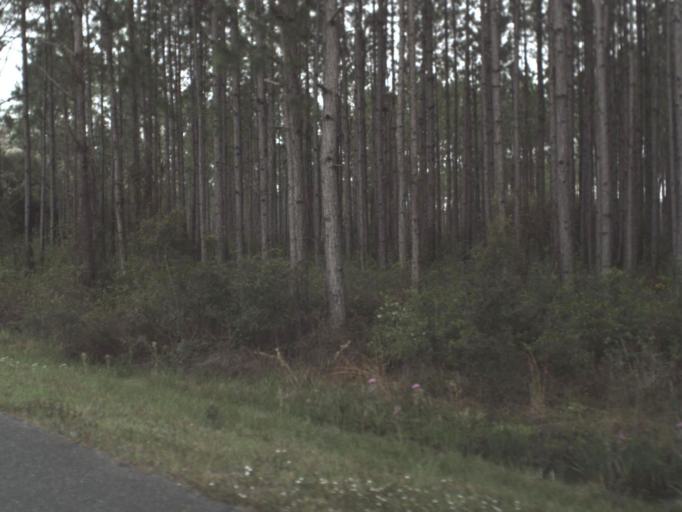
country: US
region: Florida
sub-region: Franklin County
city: Eastpoint
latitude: 29.8018
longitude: -84.8330
